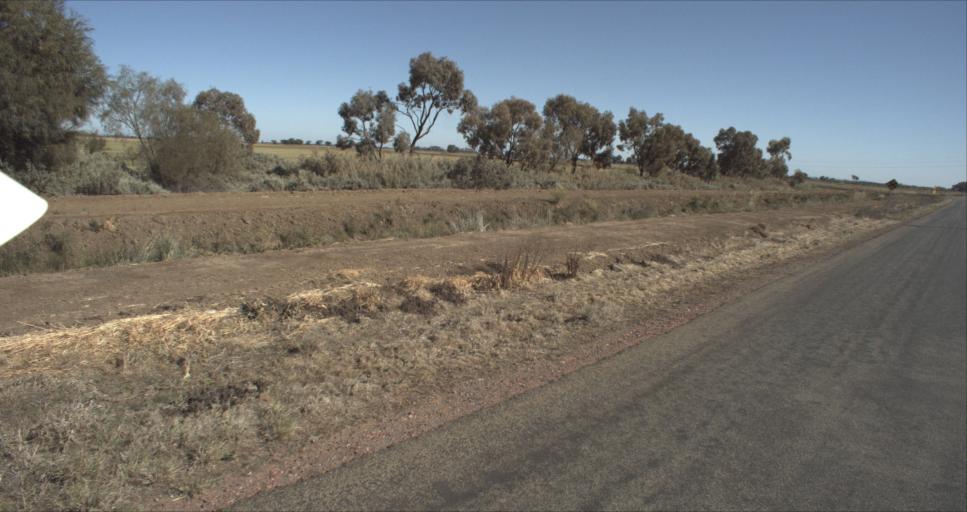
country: AU
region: New South Wales
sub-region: Leeton
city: Leeton
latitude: -34.5519
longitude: 146.2672
